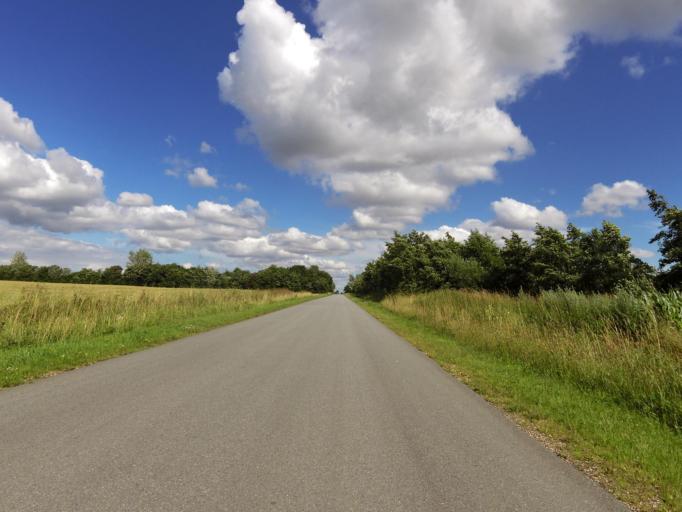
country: DK
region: South Denmark
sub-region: Vejen Kommune
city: Rodding
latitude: 55.3159
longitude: 9.1767
